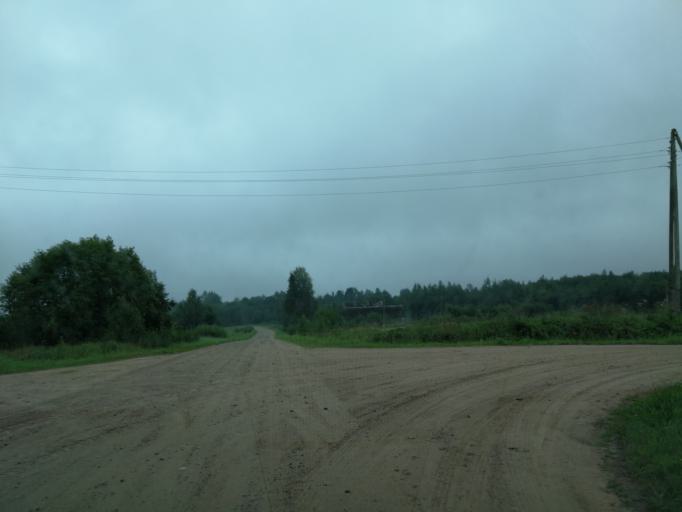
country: LV
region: Preilu Rajons
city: Jaunaglona
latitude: 56.3228
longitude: 27.0365
